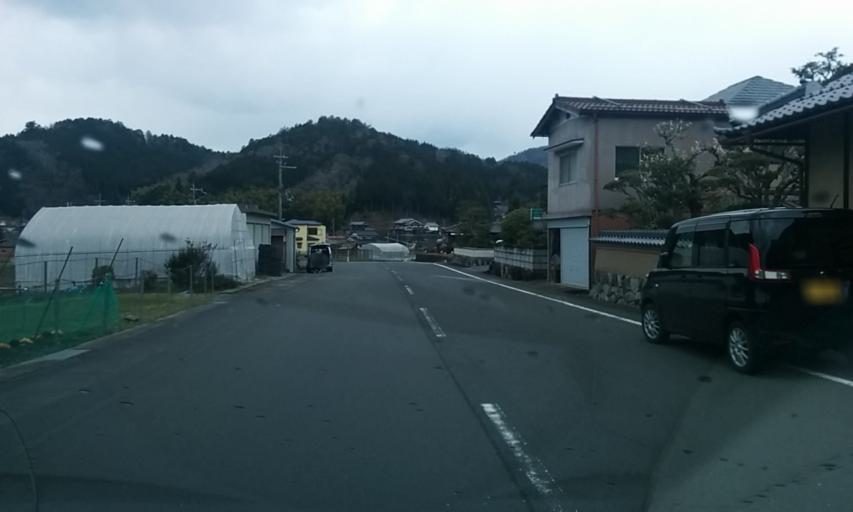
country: JP
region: Hyogo
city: Sasayama
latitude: 35.1251
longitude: 135.4147
